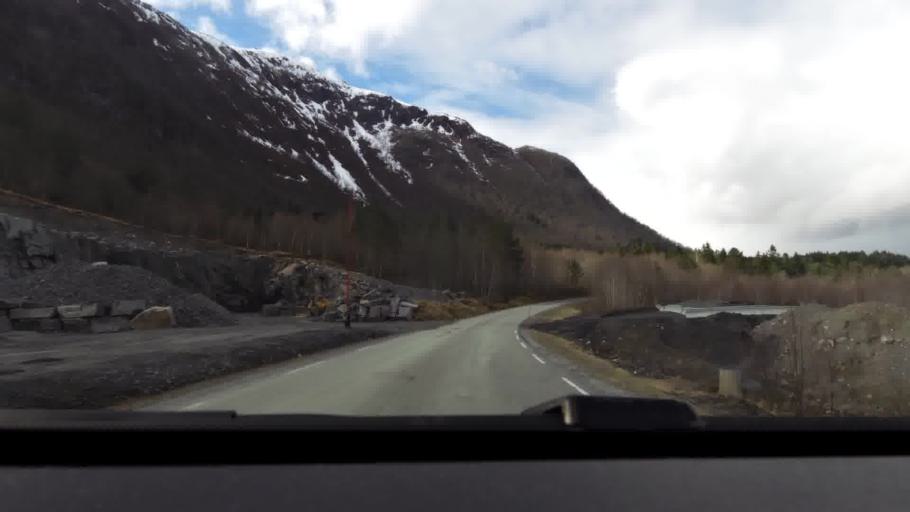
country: NO
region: More og Romsdal
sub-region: Averoy
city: Bruhagen
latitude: 63.0999
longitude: 7.6273
